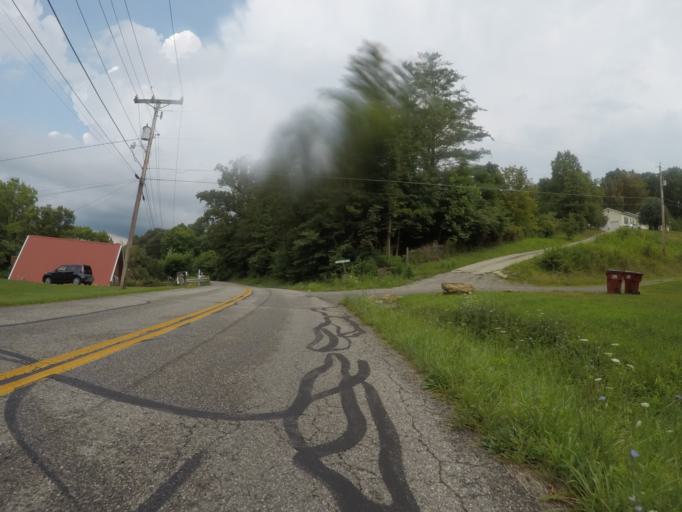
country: US
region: Kentucky
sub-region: Boyd County
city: Meads
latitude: 38.4057
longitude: -82.6603
